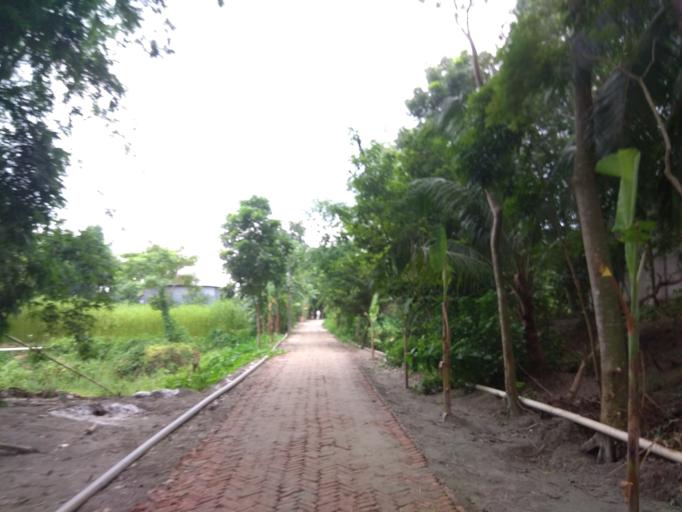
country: BD
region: Dhaka
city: Dohar
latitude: 23.4916
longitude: 90.0378
